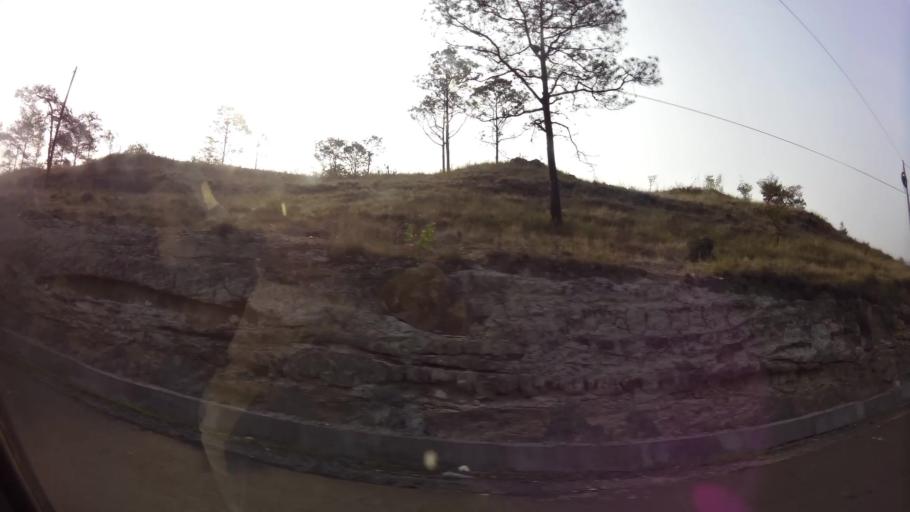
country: HN
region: Francisco Morazan
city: Zambrano
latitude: 14.2360
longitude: -87.3880
